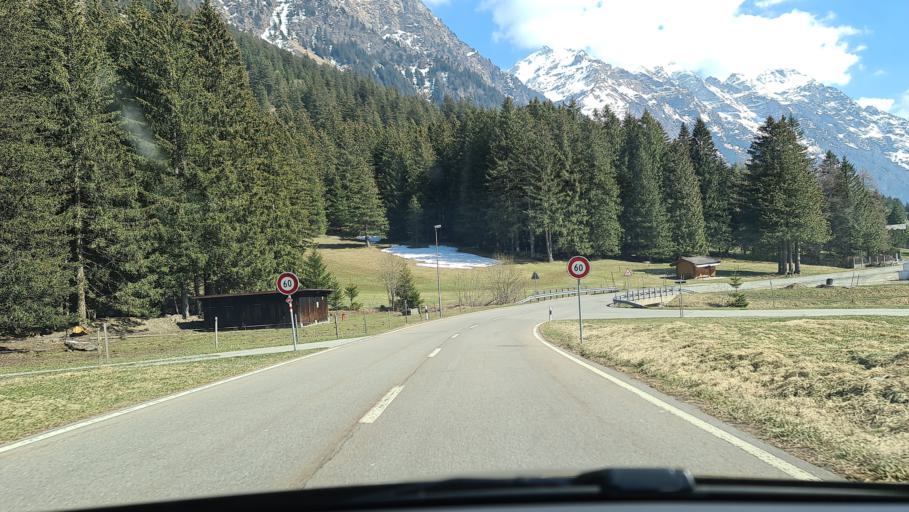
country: CH
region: Grisons
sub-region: Moesa District
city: Mesocco
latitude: 46.4270
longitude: 9.2230
